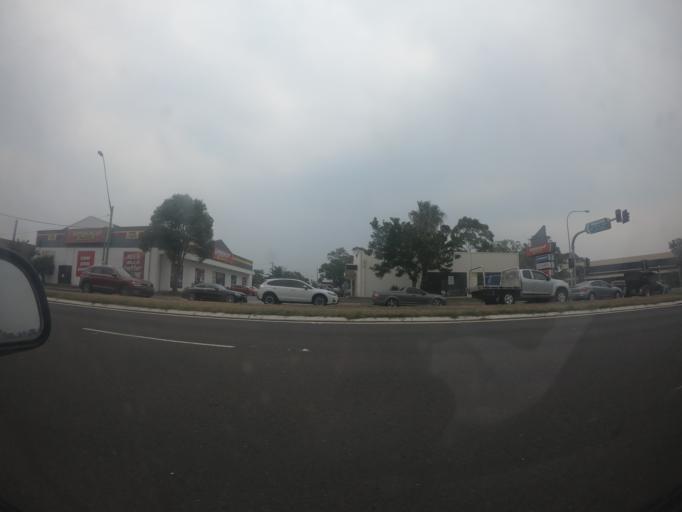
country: AU
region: New South Wales
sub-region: Shellharbour
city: Lake Illawarra
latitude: -34.5528
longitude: 150.8600
